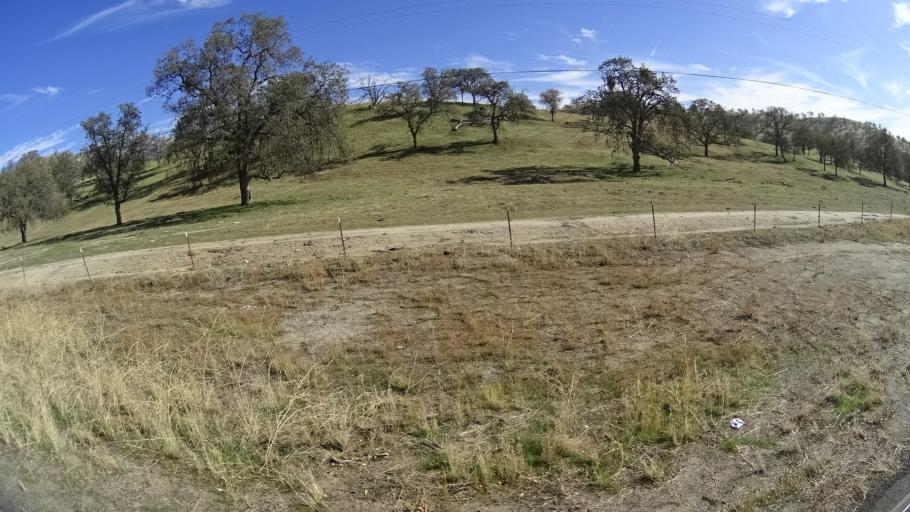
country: US
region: California
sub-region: Kern County
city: Oildale
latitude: 35.6391
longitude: -118.8374
